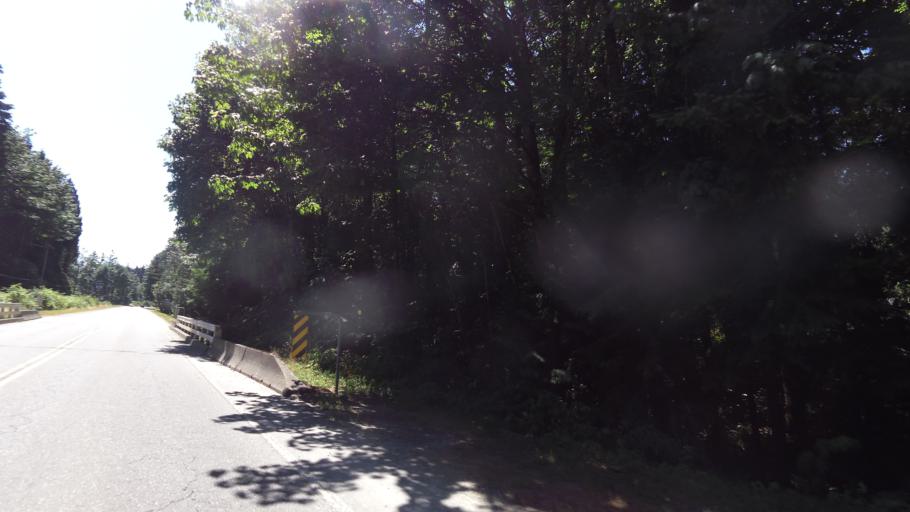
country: CA
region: British Columbia
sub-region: Fraser Valley Regional District
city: Chilliwack
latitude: 49.2353
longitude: -122.0057
